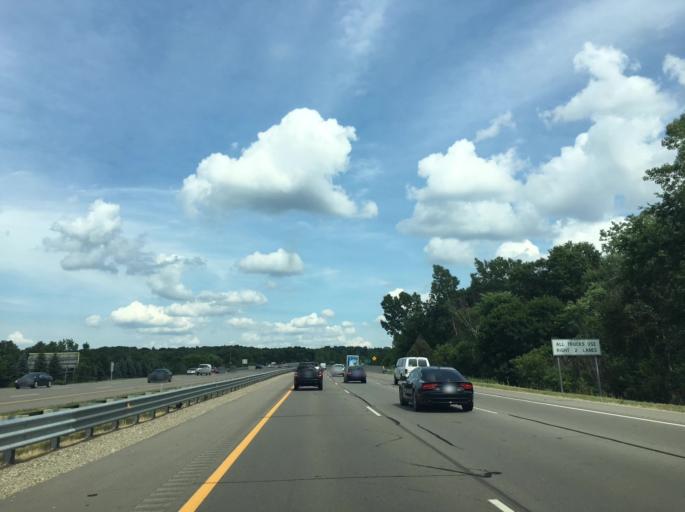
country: US
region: Michigan
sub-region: Oakland County
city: Clarkston
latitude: 42.7457
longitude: -83.4047
